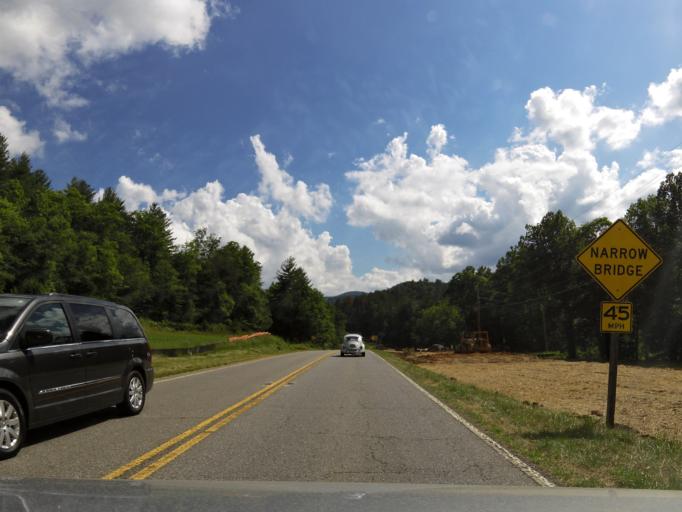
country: US
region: Georgia
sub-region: Towns County
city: Hiawassee
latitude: 34.8614
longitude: -83.7197
